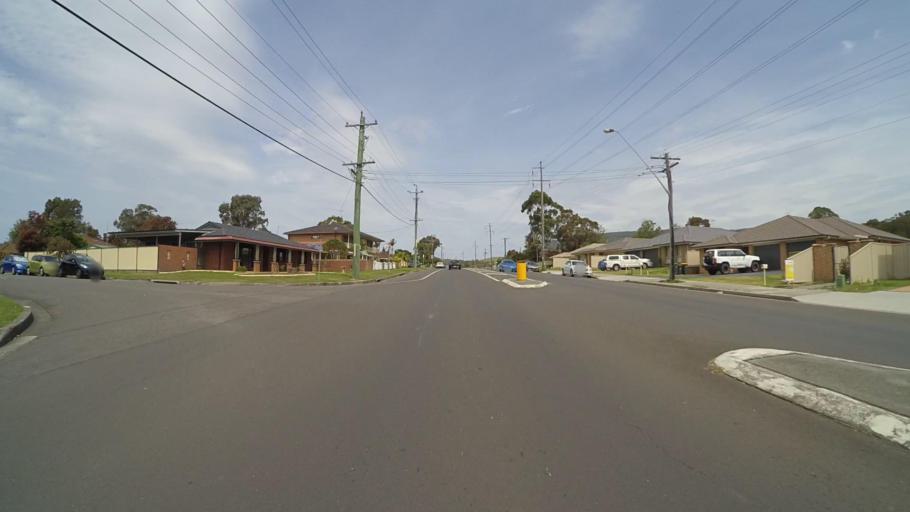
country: AU
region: New South Wales
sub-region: Shellharbour
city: Albion Park Rail
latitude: -34.5762
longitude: 150.7766
